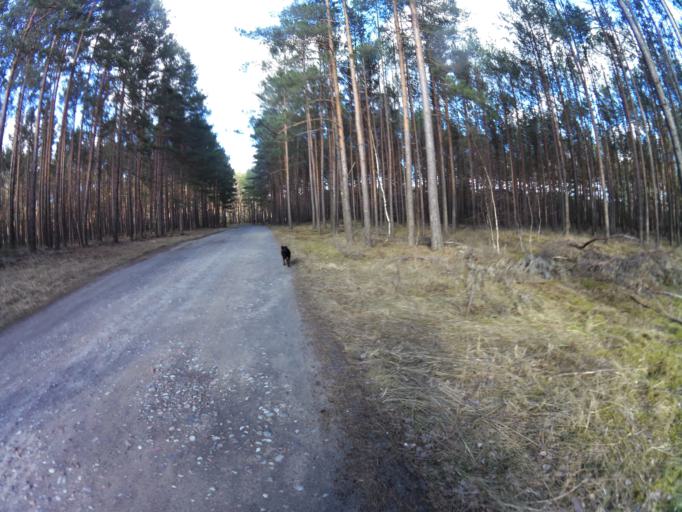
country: PL
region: West Pomeranian Voivodeship
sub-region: Powiat mysliborski
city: Debno
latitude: 52.7875
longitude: 14.7477
